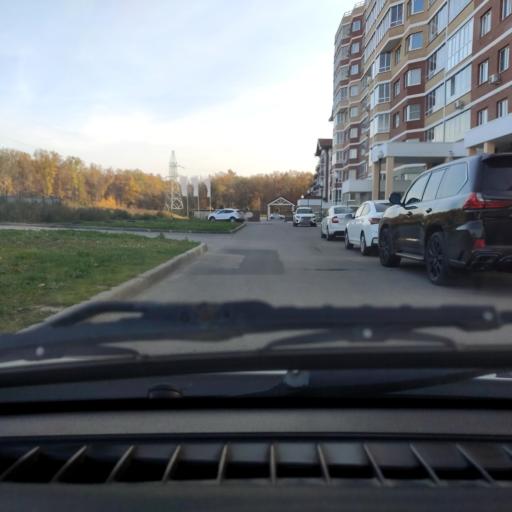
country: RU
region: Samara
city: Tol'yatti
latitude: 53.4994
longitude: 49.4215
